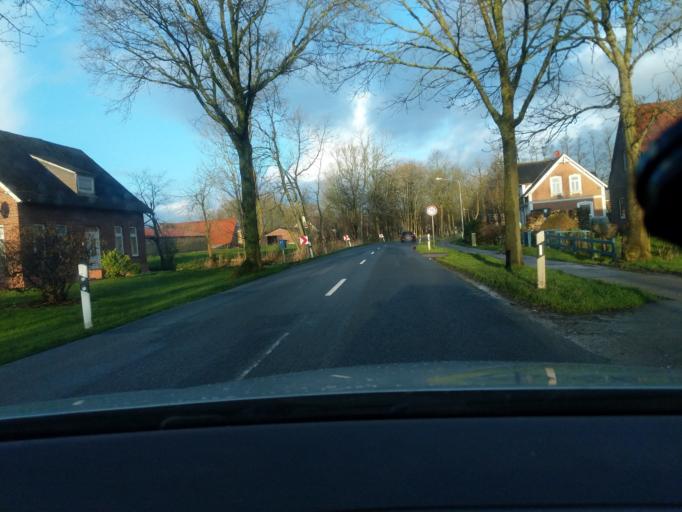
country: DE
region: Lower Saxony
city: Cuxhaven
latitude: 53.8267
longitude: 8.7327
